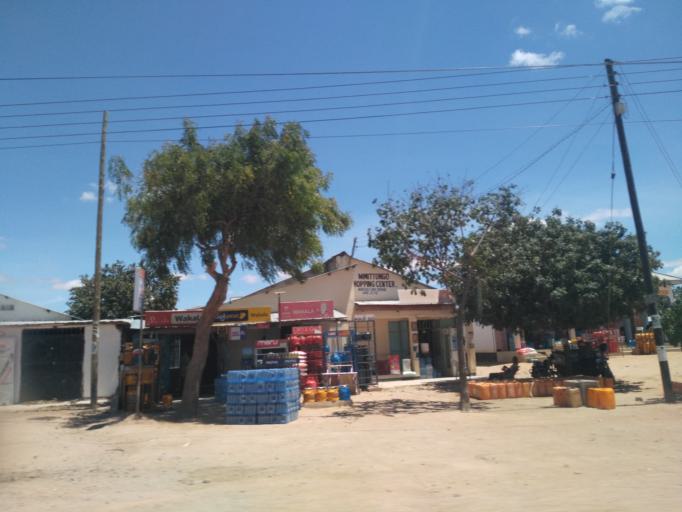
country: TZ
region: Dodoma
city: Kisasa
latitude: -6.1886
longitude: 35.7768
